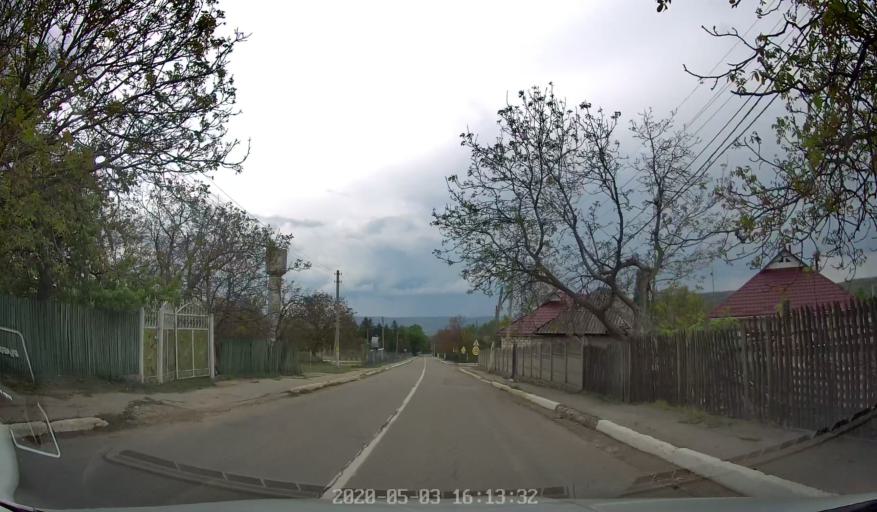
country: MD
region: Calarasi
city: Calarasi
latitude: 47.1972
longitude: 28.3433
